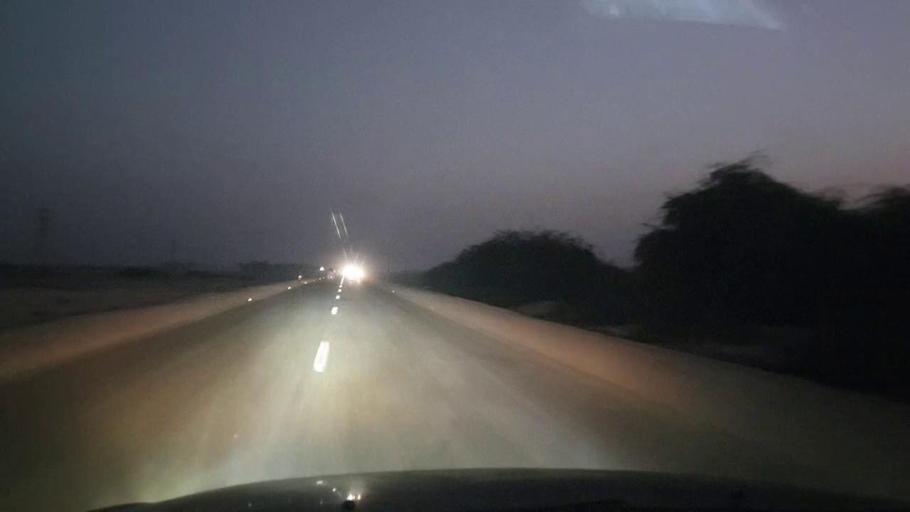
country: PK
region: Sindh
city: Chambar
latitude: 25.3499
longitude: 68.7904
